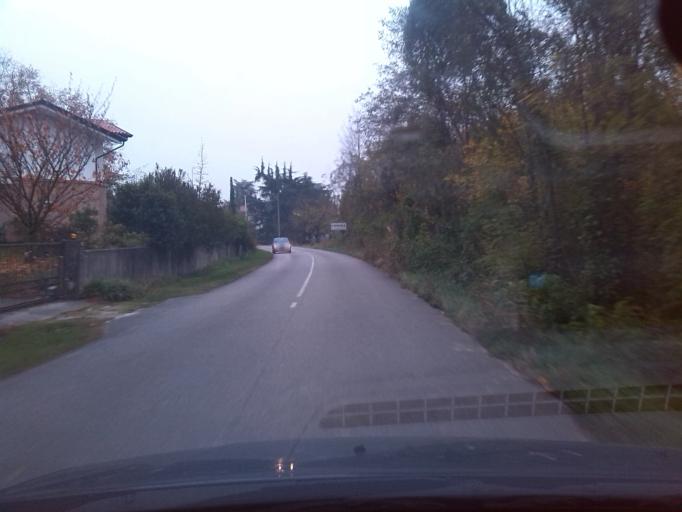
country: IT
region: Friuli Venezia Giulia
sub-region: Provincia di Gorizia
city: Moraro
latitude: 45.9260
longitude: 13.4811
